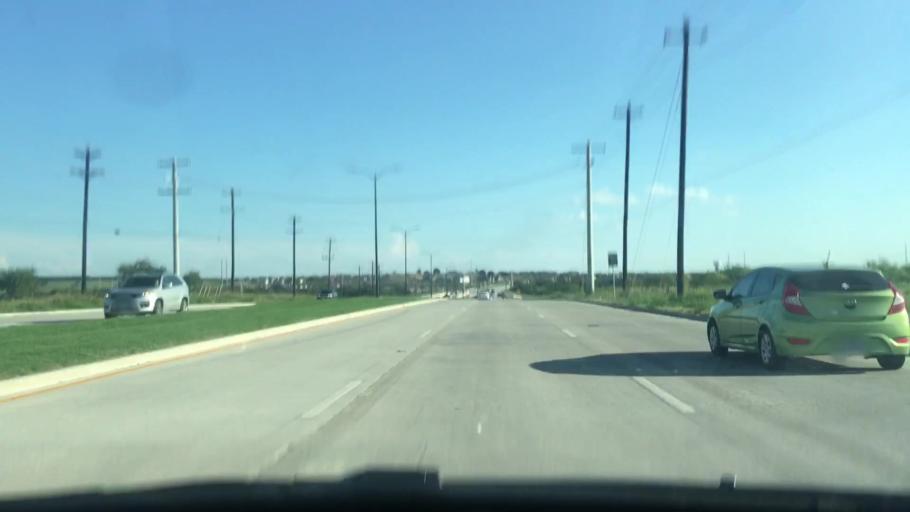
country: US
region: Texas
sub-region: Denton County
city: Little Elm
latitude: 33.2106
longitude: -96.8805
